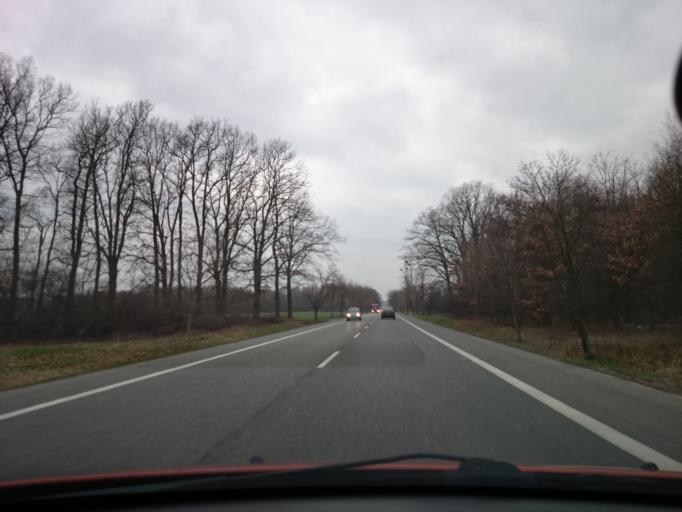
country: PL
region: Opole Voivodeship
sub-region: Powiat opolski
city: Dabrowa
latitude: 50.6902
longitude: 17.7794
